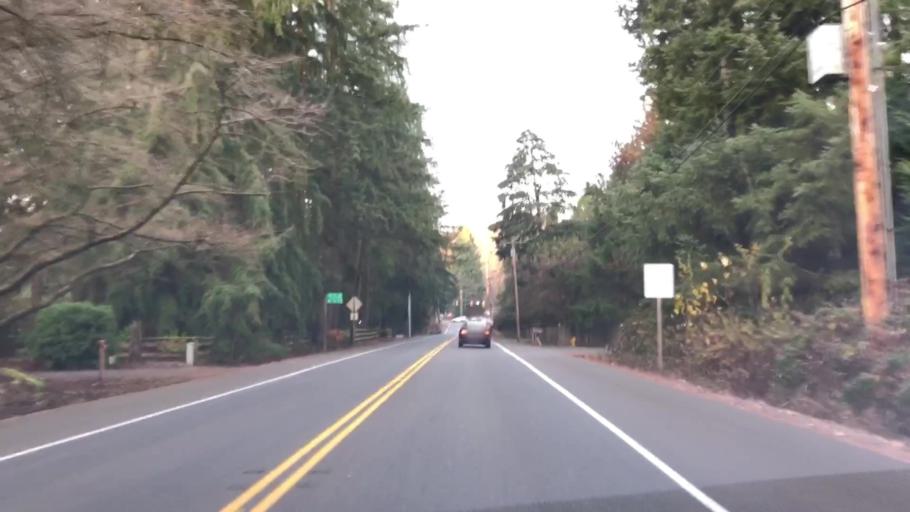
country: US
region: Washington
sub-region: King County
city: Cottage Lake
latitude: 47.7175
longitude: -122.0846
